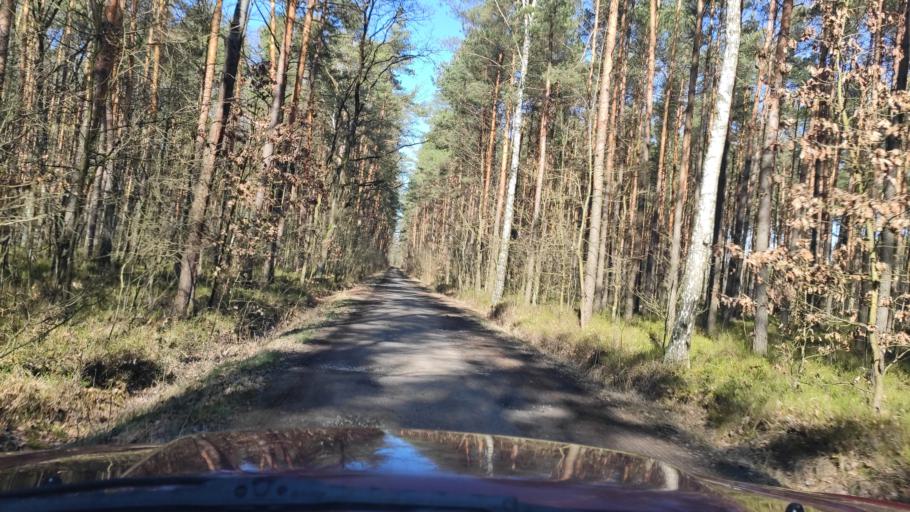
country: PL
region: Masovian Voivodeship
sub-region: Powiat kozienicki
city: Garbatka-Letnisko
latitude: 51.4373
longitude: 21.5446
